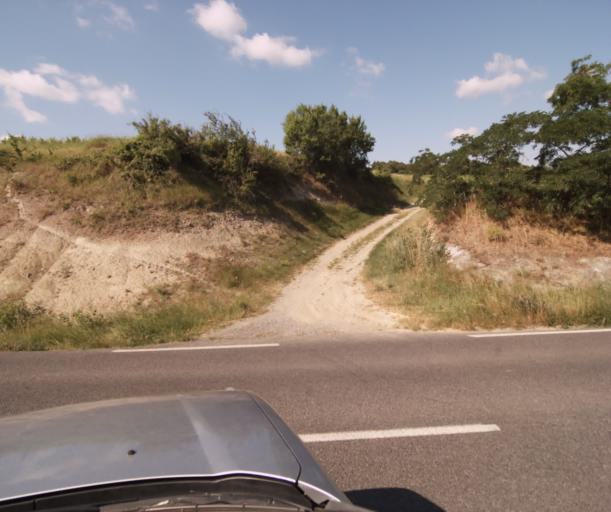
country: FR
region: Languedoc-Roussillon
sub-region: Departement de l'Aude
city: Limoux
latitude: 43.0761
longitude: 2.1964
